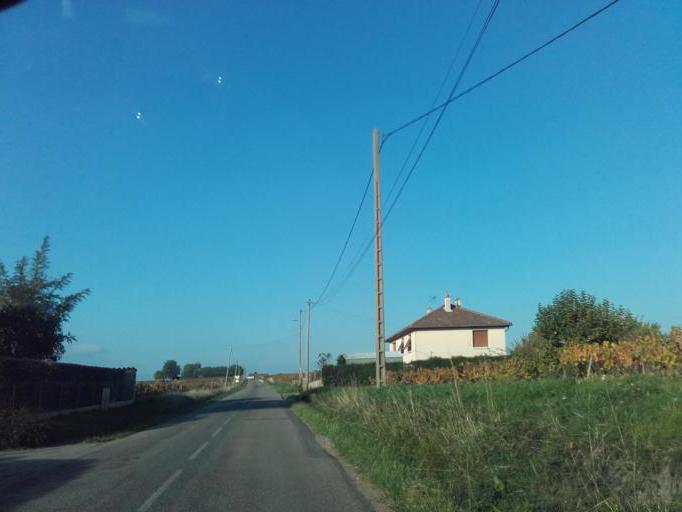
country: FR
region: Bourgogne
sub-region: Departement de Saone-et-Loire
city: La Chapelle-de-Guinchay
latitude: 46.2241
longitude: 4.7456
